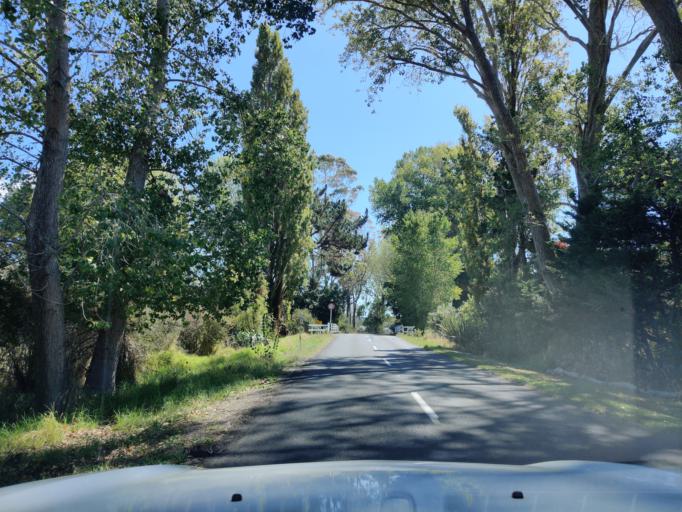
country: NZ
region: Waikato
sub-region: Thames-Coromandel District
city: Thames
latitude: -37.0524
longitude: 175.3010
